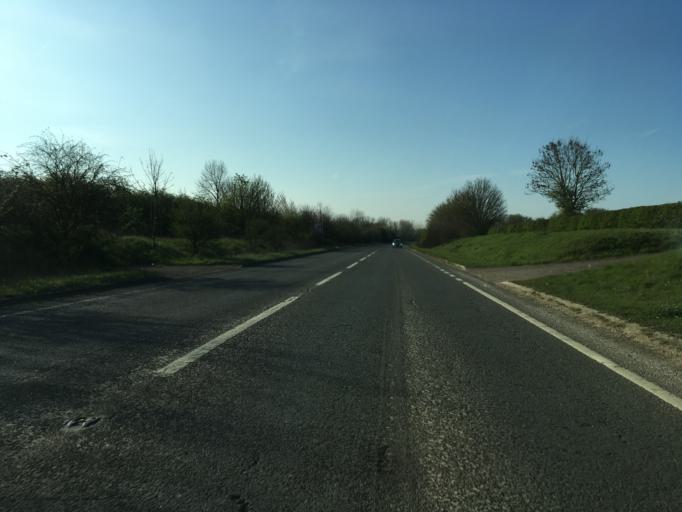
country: GB
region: England
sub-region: Milton Keynes
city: Stony Stratford
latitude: 52.0587
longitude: -0.8706
